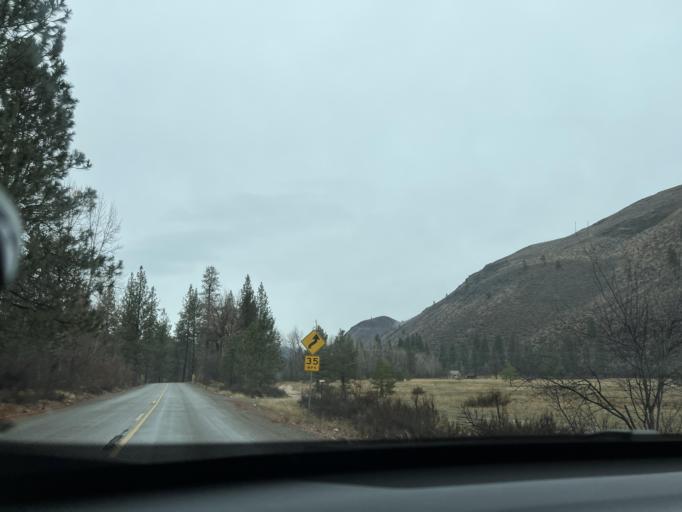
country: US
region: Washington
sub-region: Okanogan County
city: Brewster
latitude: 48.5279
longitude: -120.1800
